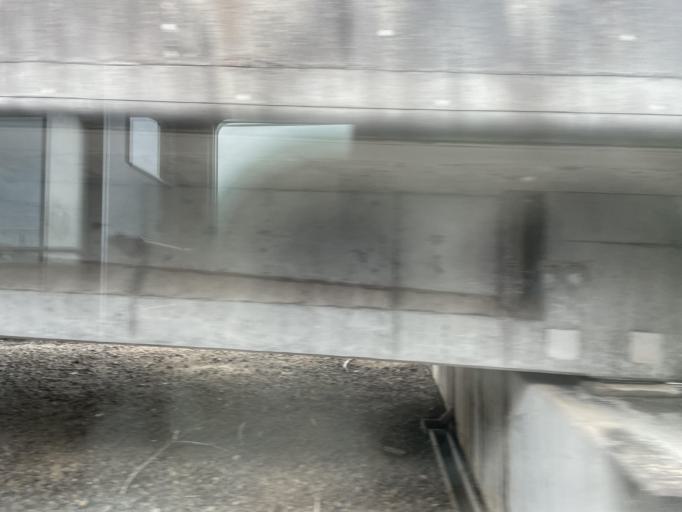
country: JP
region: Osaka
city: Kaizuka
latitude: 34.3879
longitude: 135.3288
